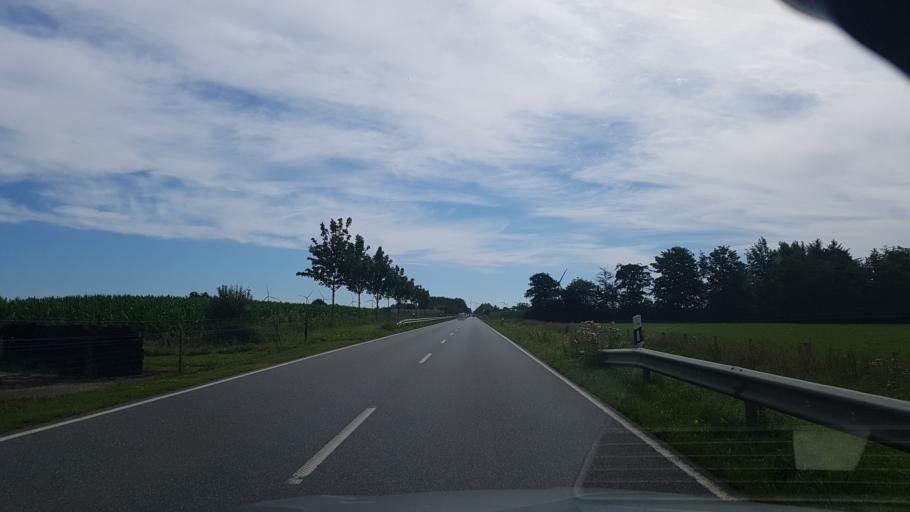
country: DE
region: Schleswig-Holstein
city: Bramstedtlund
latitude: 54.8659
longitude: 9.1011
